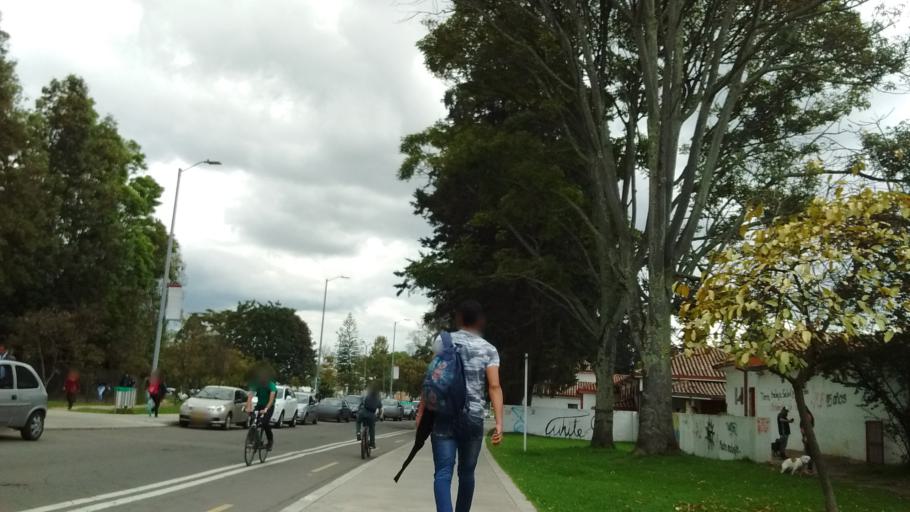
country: CO
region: Bogota D.C.
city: Bogota
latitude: 4.6349
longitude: -74.0859
